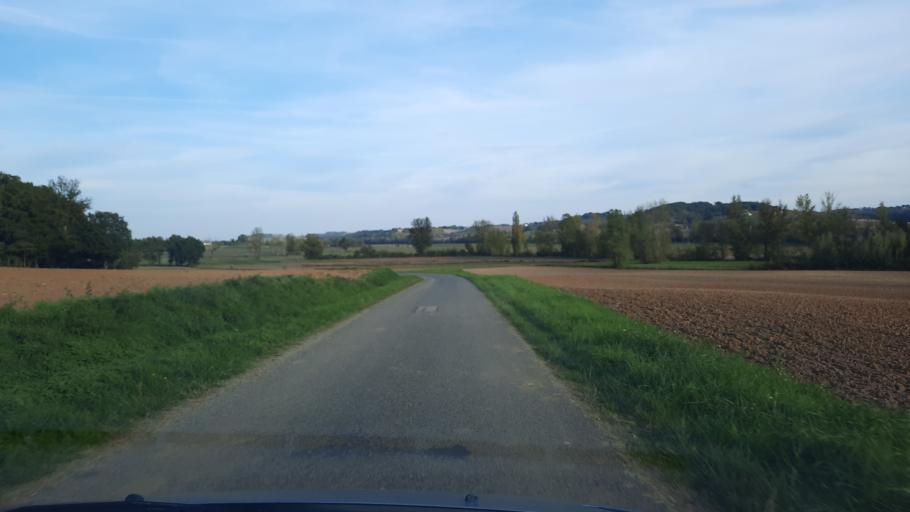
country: FR
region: Midi-Pyrenees
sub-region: Departement du Tarn-et-Garonne
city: Lafrancaise
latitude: 44.1689
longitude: 1.2800
